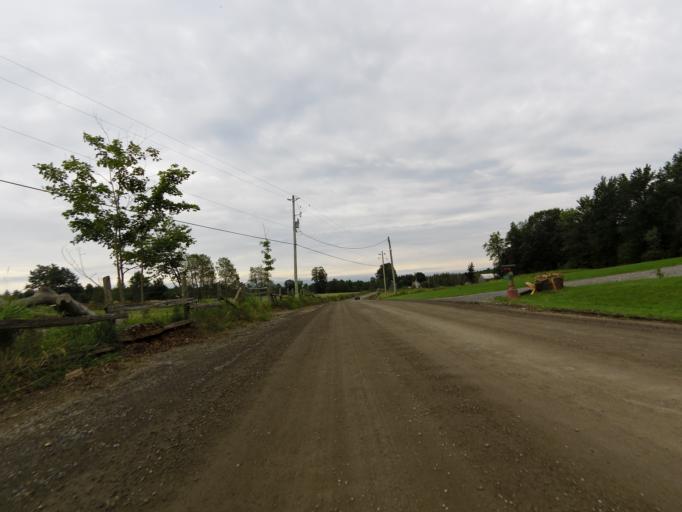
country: CA
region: Ontario
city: Kingston
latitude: 44.5845
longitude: -76.6353
